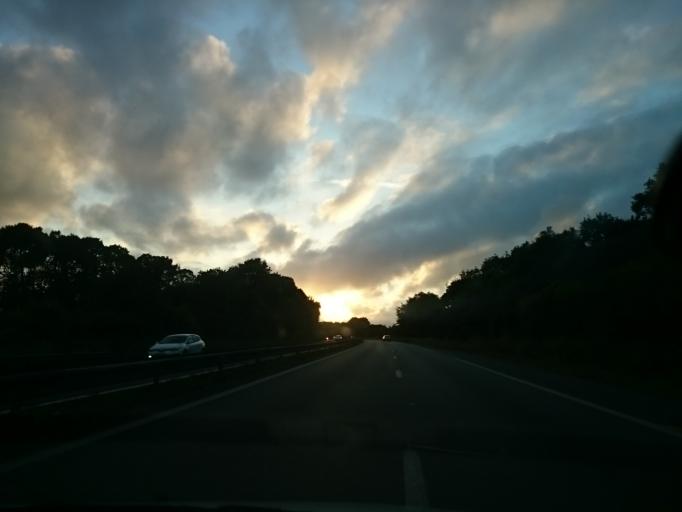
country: FR
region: Brittany
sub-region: Departement du Morbihan
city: Queven
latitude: 47.7748
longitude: -3.3919
